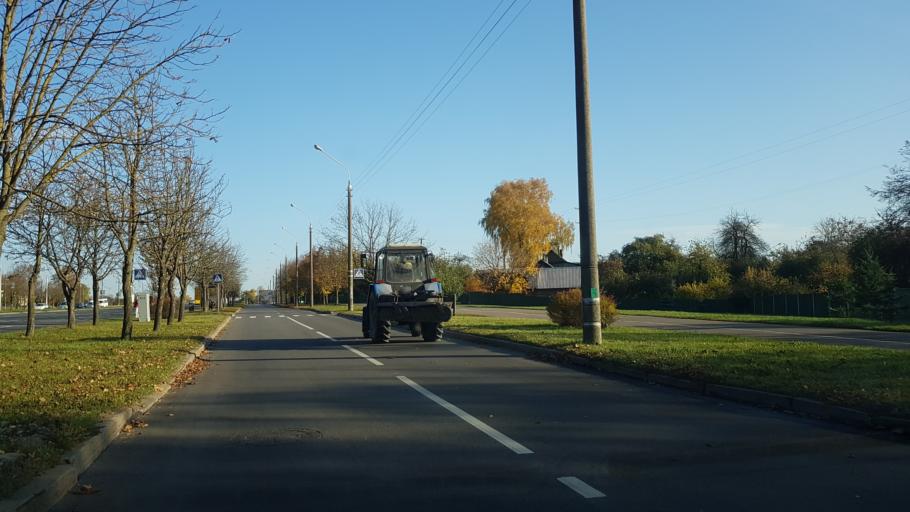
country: BY
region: Minsk
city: Syenitsa
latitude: 53.8803
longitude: 27.5095
